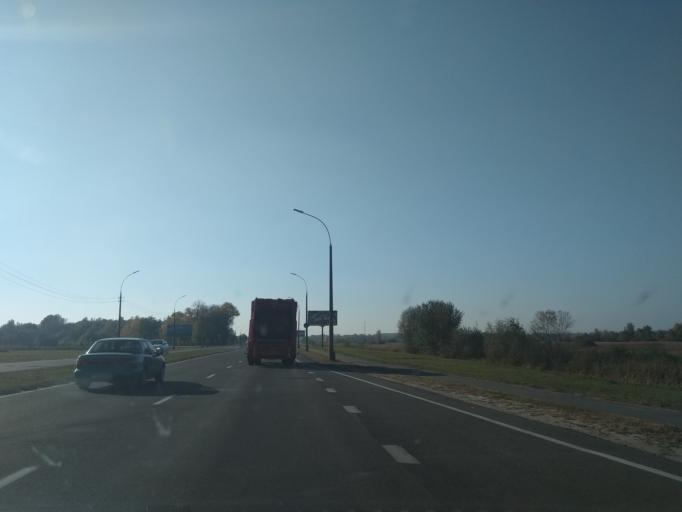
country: BY
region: Brest
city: Brest
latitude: 52.0749
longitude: 23.7014
